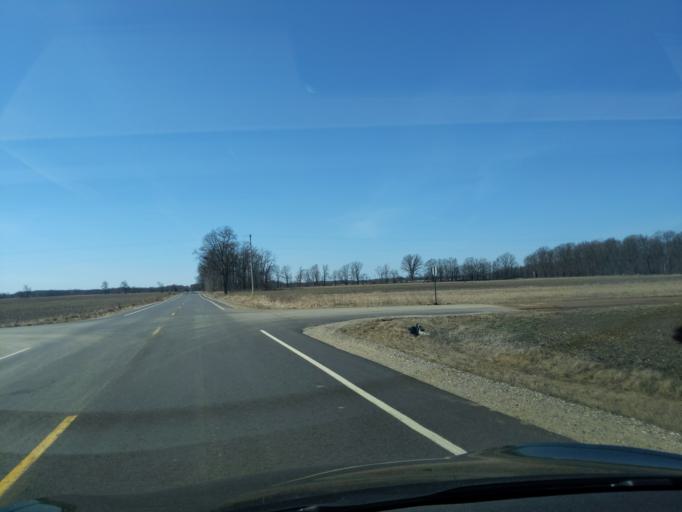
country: US
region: Michigan
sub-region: Ionia County
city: Lake Odessa
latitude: 42.7270
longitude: -85.0144
